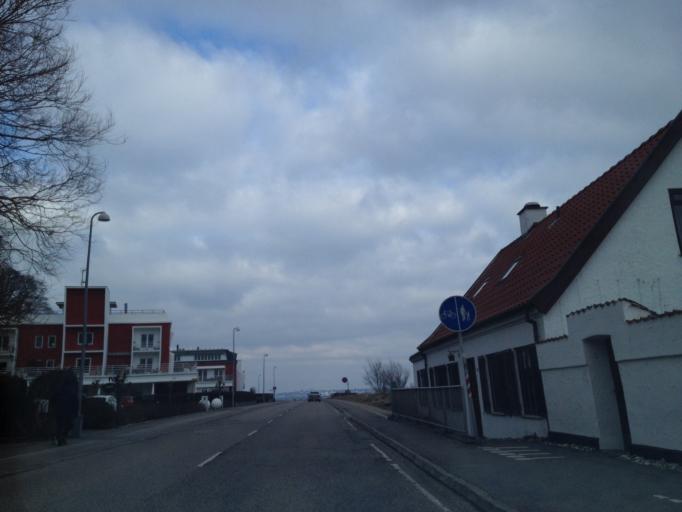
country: DK
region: Capital Region
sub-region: Helsingor Kommune
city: Espergaerde
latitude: 56.0106
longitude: 12.5930
